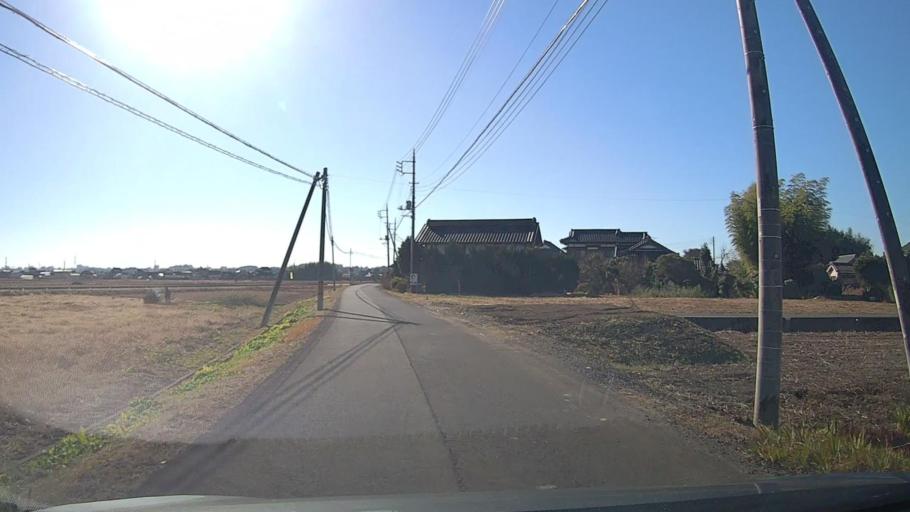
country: JP
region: Ibaraki
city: Mito-shi
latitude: 36.4291
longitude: 140.4474
